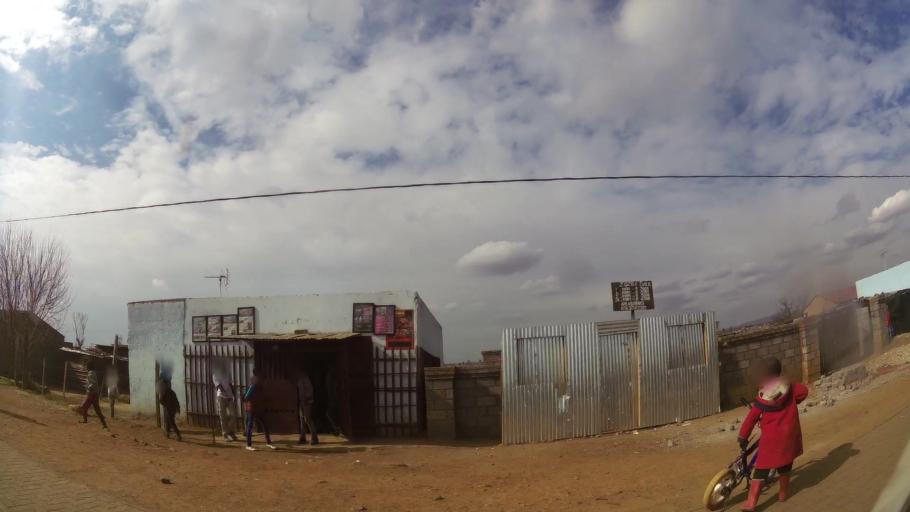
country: ZA
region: Gauteng
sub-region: Ekurhuleni Metropolitan Municipality
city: Germiston
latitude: -26.4134
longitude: 28.1655
